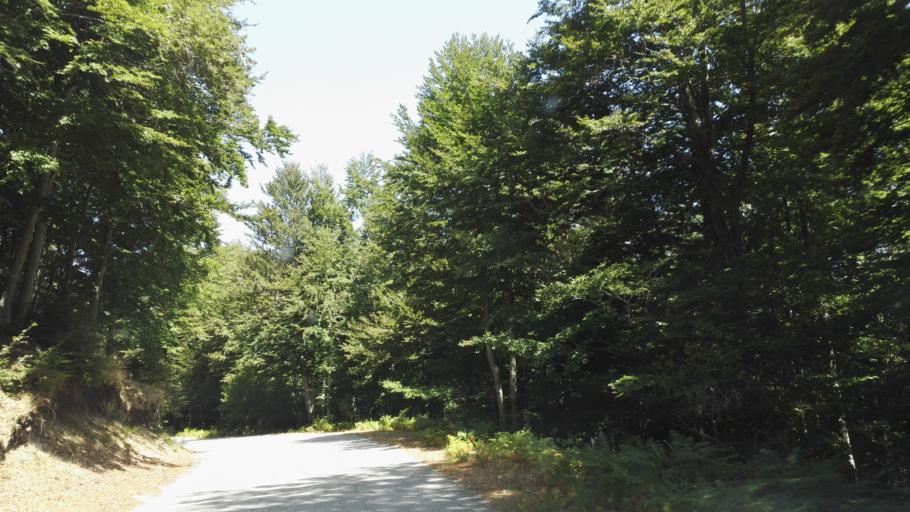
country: IT
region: Calabria
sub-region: Provincia di Vibo-Valentia
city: Nardodipace
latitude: 38.4903
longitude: 16.3677
